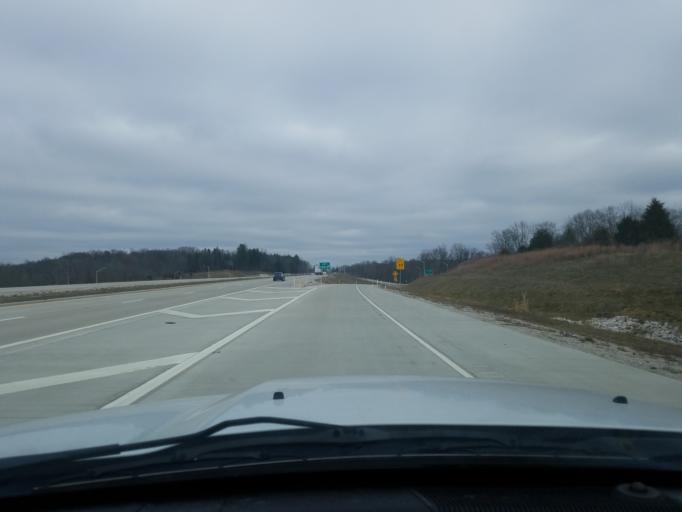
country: US
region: Indiana
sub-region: Lawrence County
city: Oolitic
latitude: 39.0318
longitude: -86.6911
